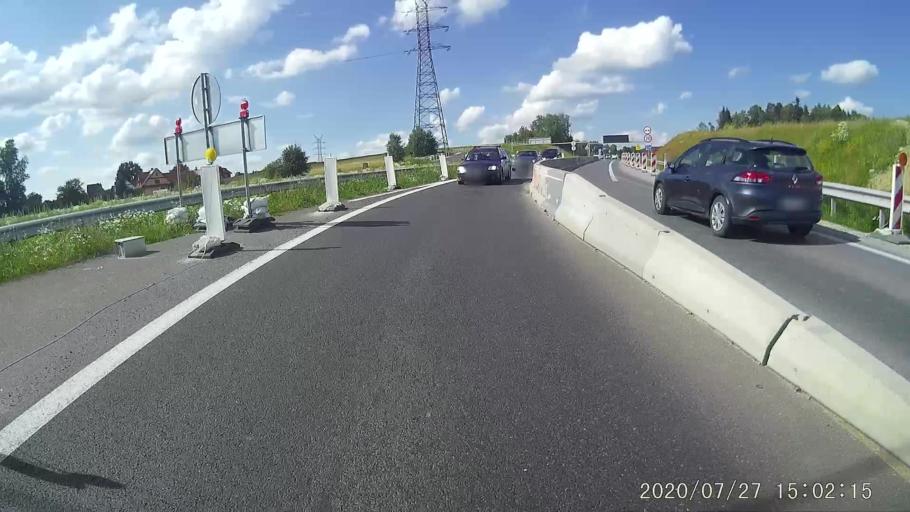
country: PL
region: Lesser Poland Voivodeship
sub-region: Powiat suski
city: Naprawa
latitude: 49.6736
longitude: 19.8880
